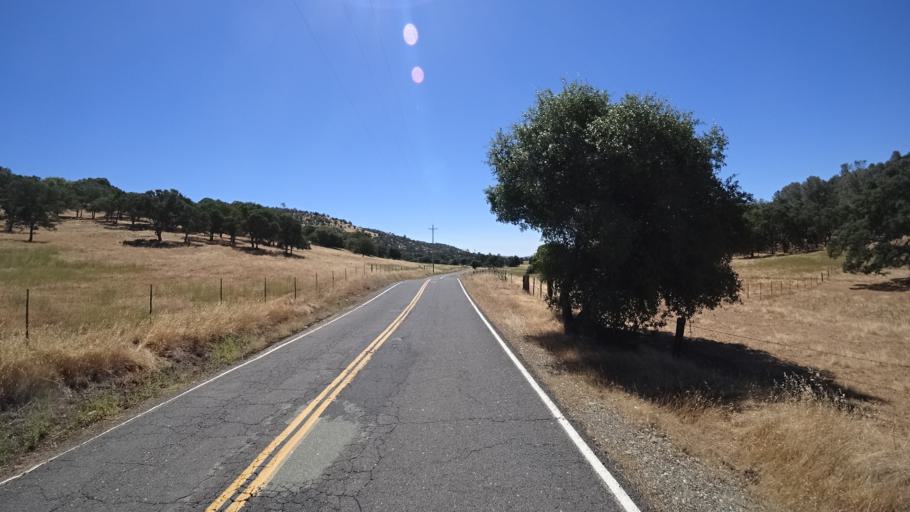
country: US
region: California
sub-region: Calaveras County
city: Copperopolis
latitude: 37.9989
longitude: -120.6593
